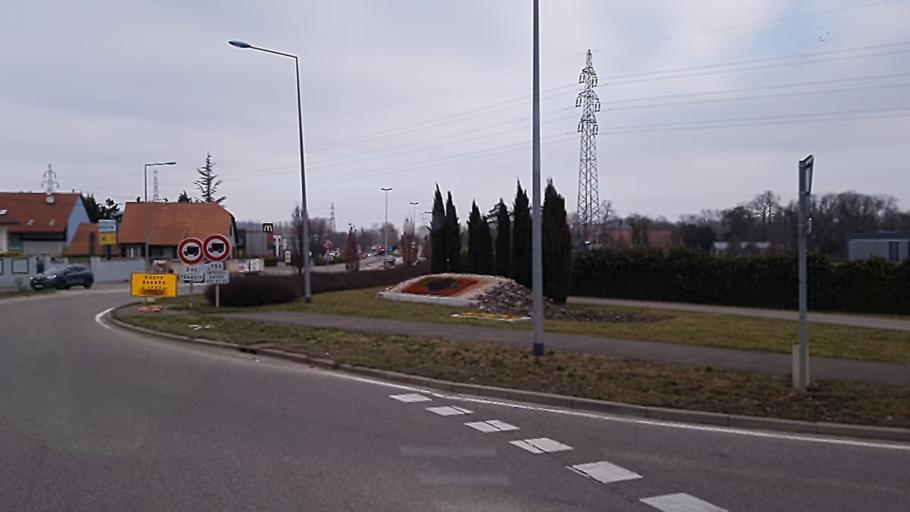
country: FR
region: Alsace
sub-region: Departement du Bas-Rhin
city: Dorlisheim
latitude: 48.5237
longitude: 7.4983
